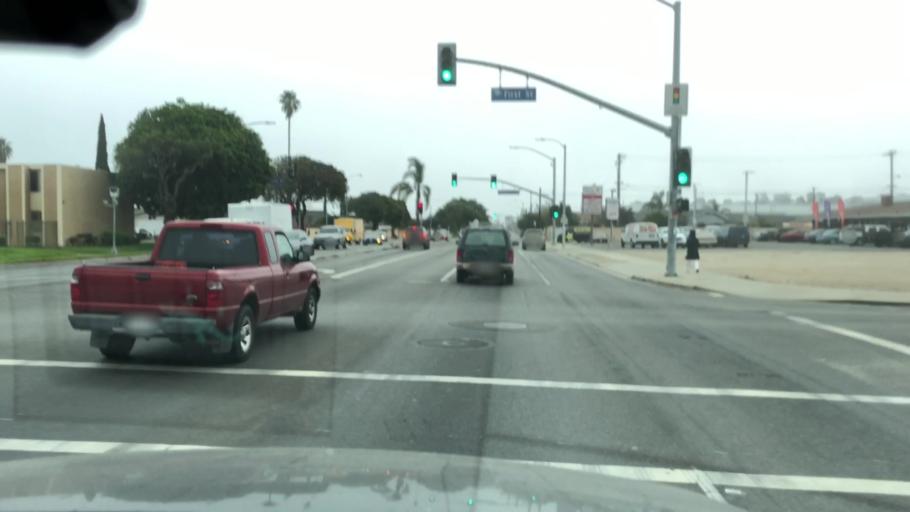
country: US
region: California
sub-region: Ventura County
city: Oxnard
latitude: 34.2027
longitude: -119.1598
